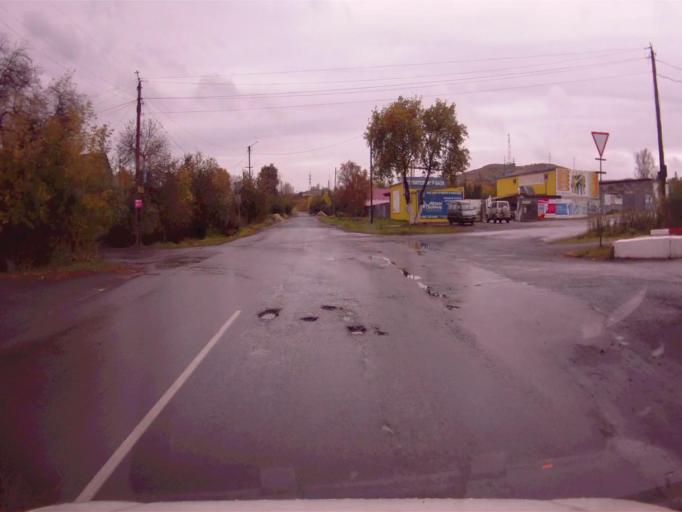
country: RU
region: Chelyabinsk
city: Verkhniy Ufaley
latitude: 56.0509
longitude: 60.2453
